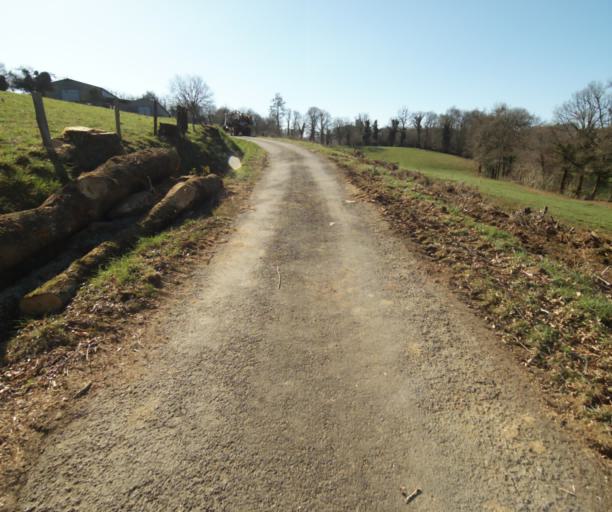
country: FR
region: Limousin
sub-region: Departement de la Correze
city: Chamboulive
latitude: 45.4059
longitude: 1.7425
